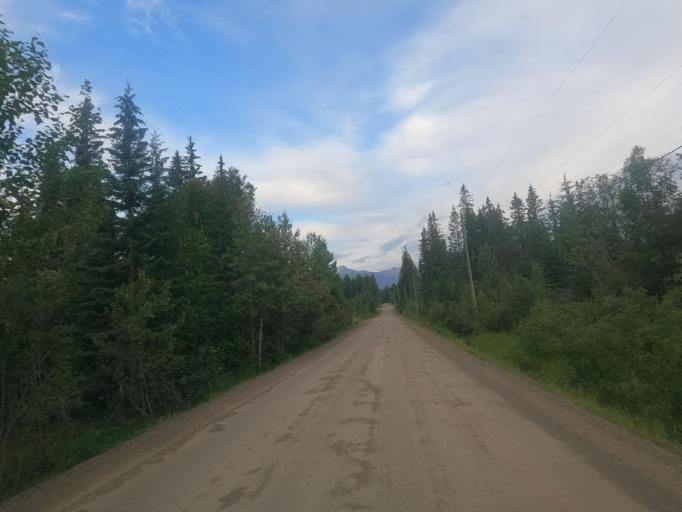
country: CA
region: British Columbia
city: Golden
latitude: 51.4385
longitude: -117.0503
